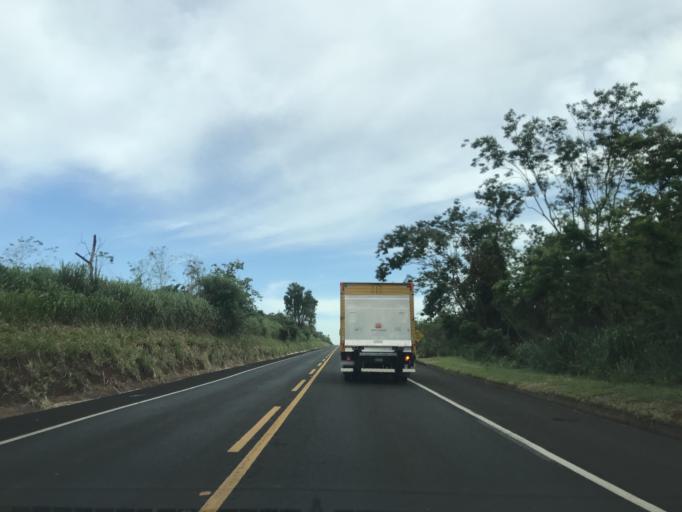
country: BR
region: Parana
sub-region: Paranavai
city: Paranavai
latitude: -22.9985
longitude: -52.5715
